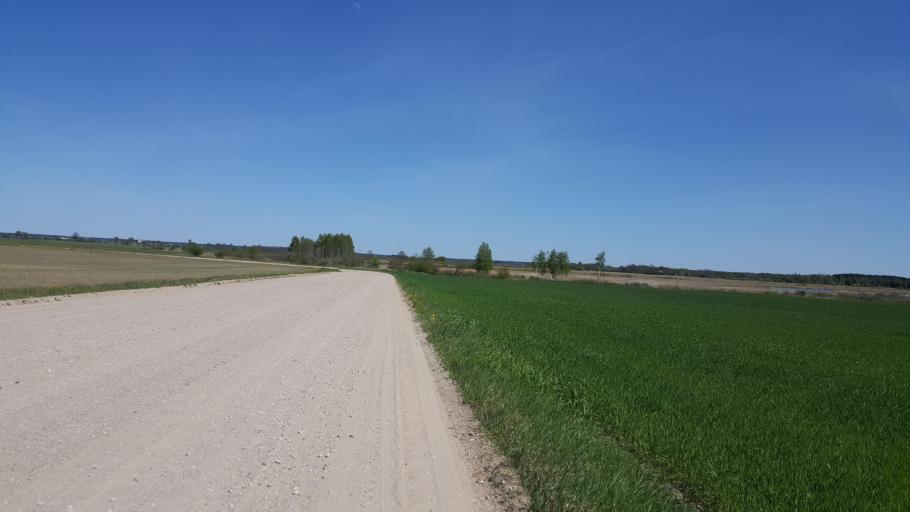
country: BY
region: Brest
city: Kamyanyets
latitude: 52.4462
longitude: 23.8614
